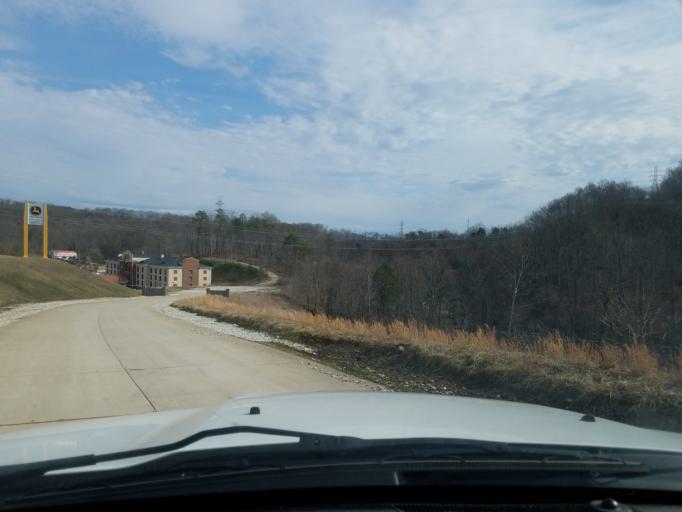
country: US
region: West Virginia
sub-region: Kanawha County
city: Cross Lanes
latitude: 38.4075
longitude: -81.7984
